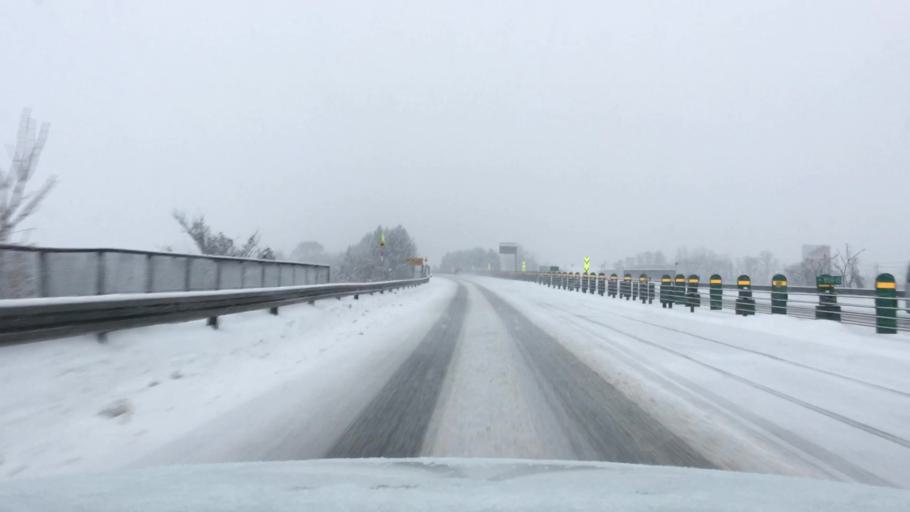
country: JP
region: Akita
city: Hanawa
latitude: 40.2587
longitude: 140.7669
